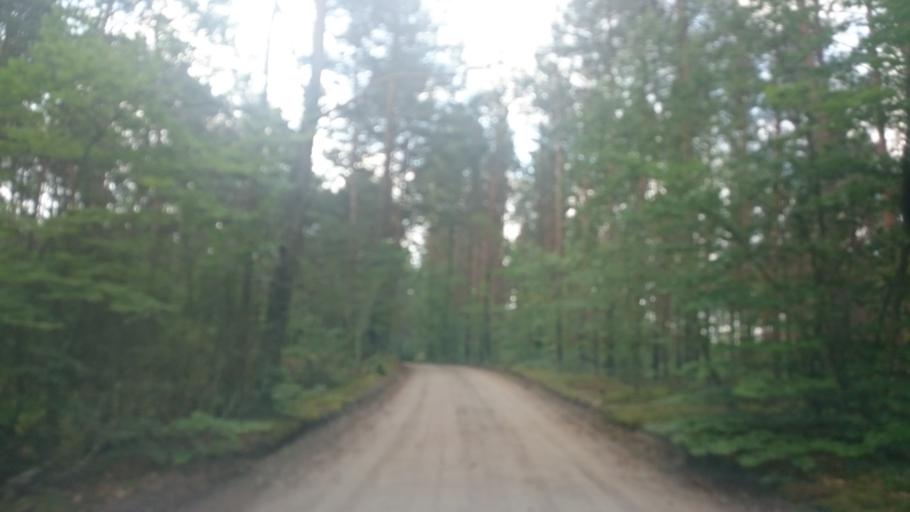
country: PL
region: Pomeranian Voivodeship
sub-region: Powiat koscierski
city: Karsin
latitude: 53.9985
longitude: 17.9327
